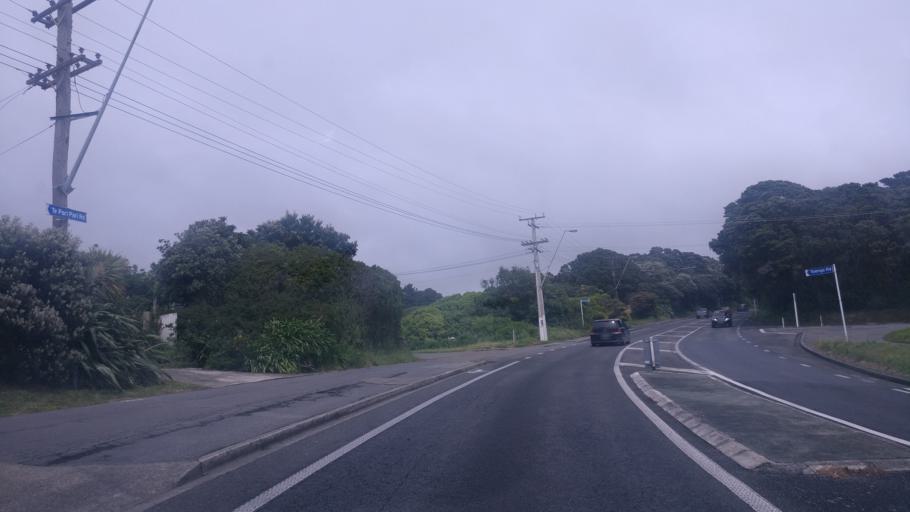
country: NZ
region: Wellington
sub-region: Porirua City
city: Porirua
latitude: -41.0323
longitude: 174.8961
